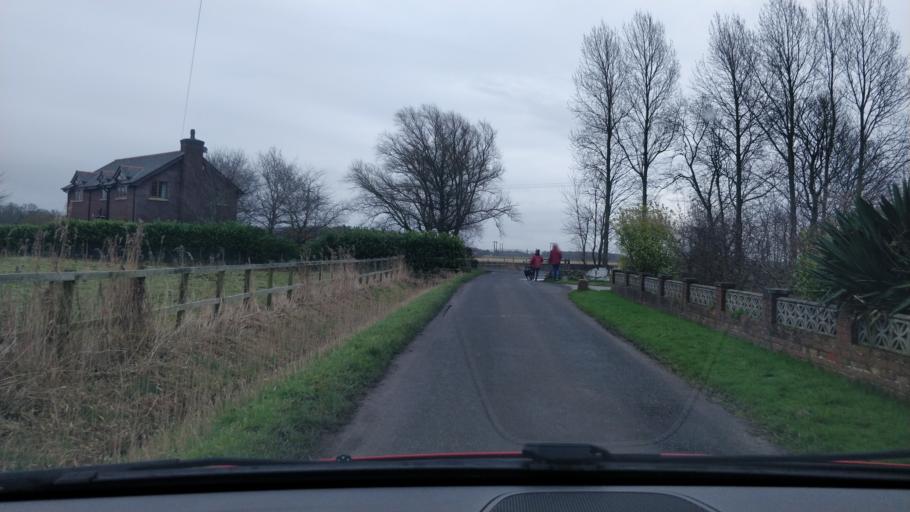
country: GB
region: England
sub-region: Lancashire
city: Banks
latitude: 53.6797
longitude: -2.9117
